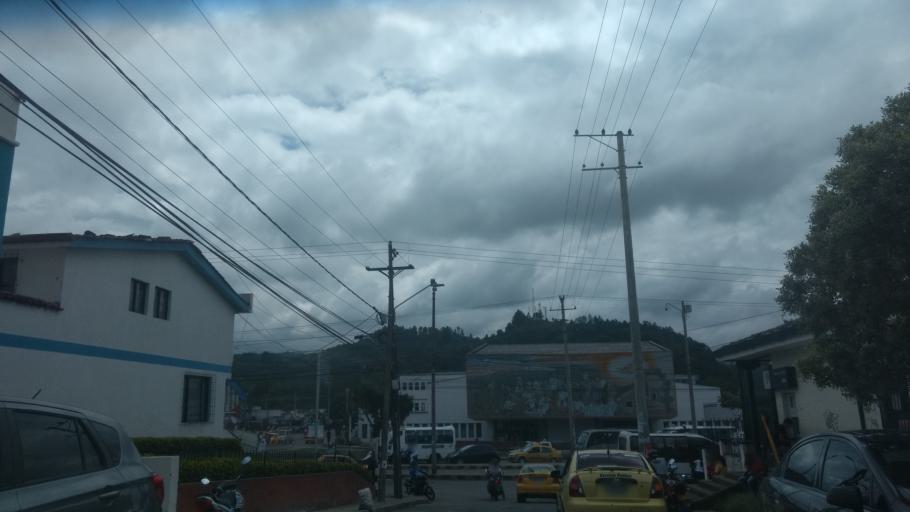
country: CO
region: Cauca
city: Popayan
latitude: 2.4519
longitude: -76.5994
